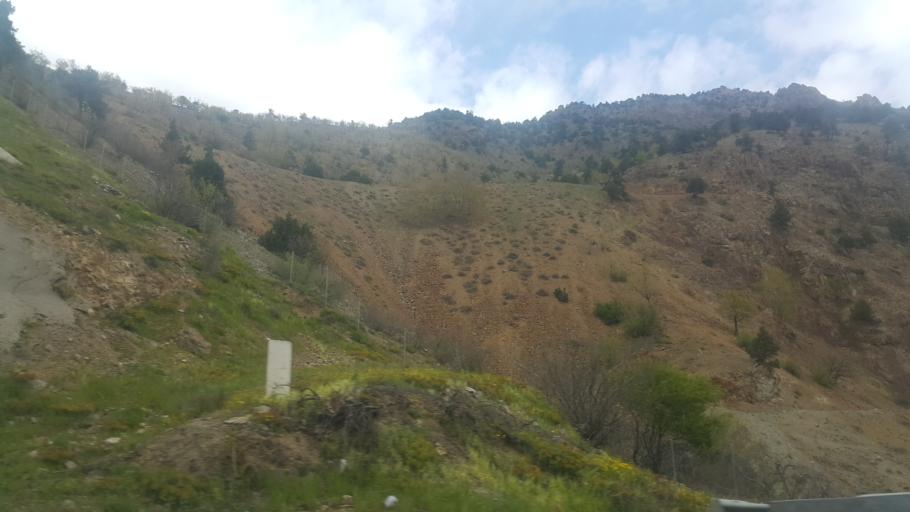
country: TR
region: Nigde
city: Ciftehan
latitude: 37.5353
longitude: 34.8007
